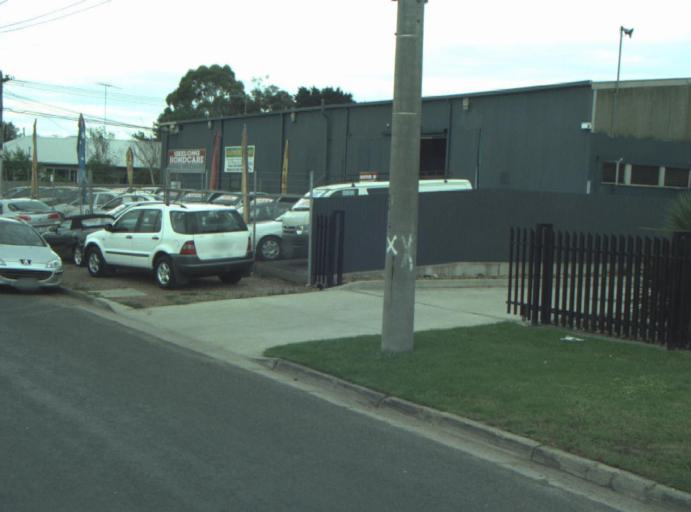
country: AU
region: Victoria
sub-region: Greater Geelong
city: Breakwater
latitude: -38.1830
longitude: 144.3666
